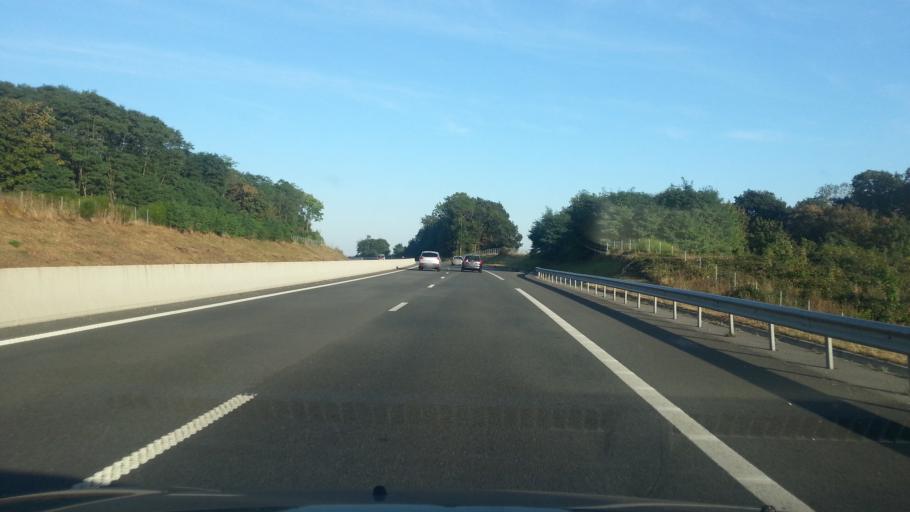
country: FR
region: Picardie
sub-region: Departement de l'Oise
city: Breuil-le-Sec
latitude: 49.3844
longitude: 2.4769
